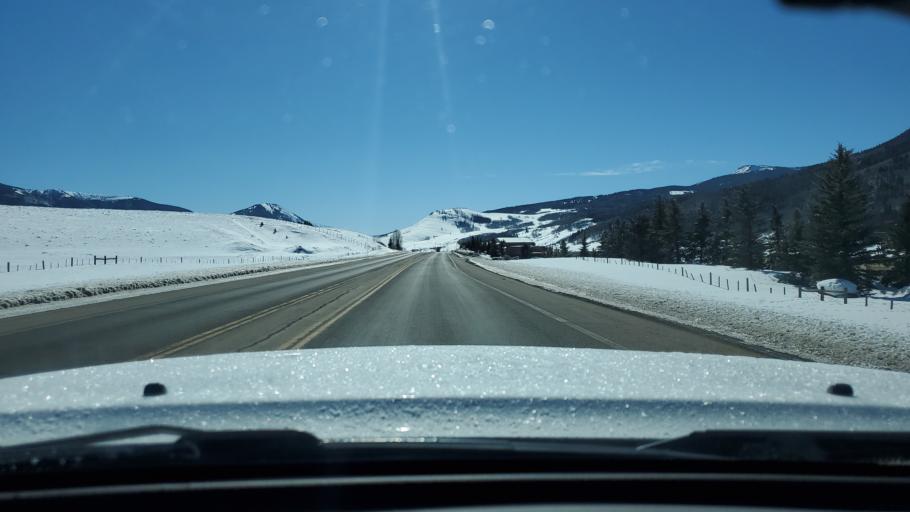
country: US
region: Colorado
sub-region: Gunnison County
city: Crested Butte
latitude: 38.8458
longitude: -106.9448
